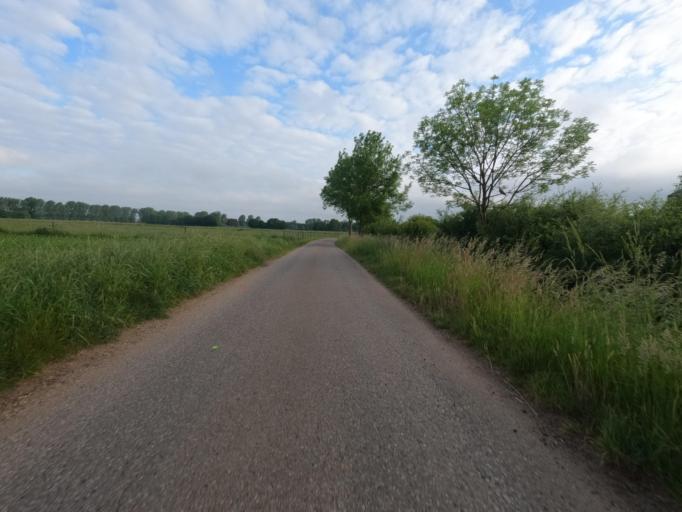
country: NL
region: Limburg
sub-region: Gemeente Roerdalen
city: Vlodrop
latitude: 51.1120
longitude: 6.0955
